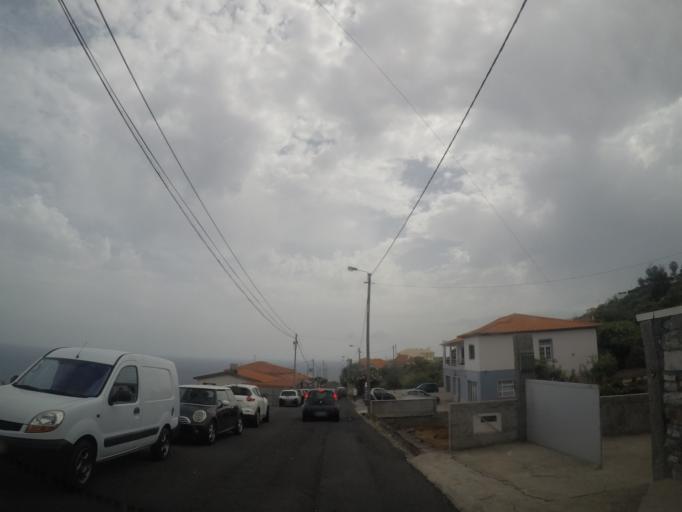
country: PT
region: Madeira
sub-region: Santa Cruz
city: Santa Cruz
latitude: 32.6583
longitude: -16.8144
